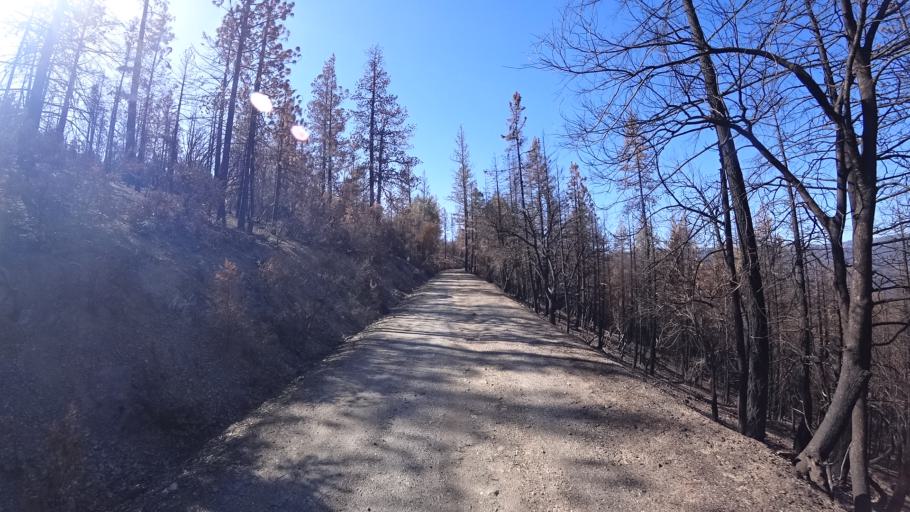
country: US
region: California
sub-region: Tehama County
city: Rancho Tehama Reserve
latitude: 39.6748
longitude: -122.7086
